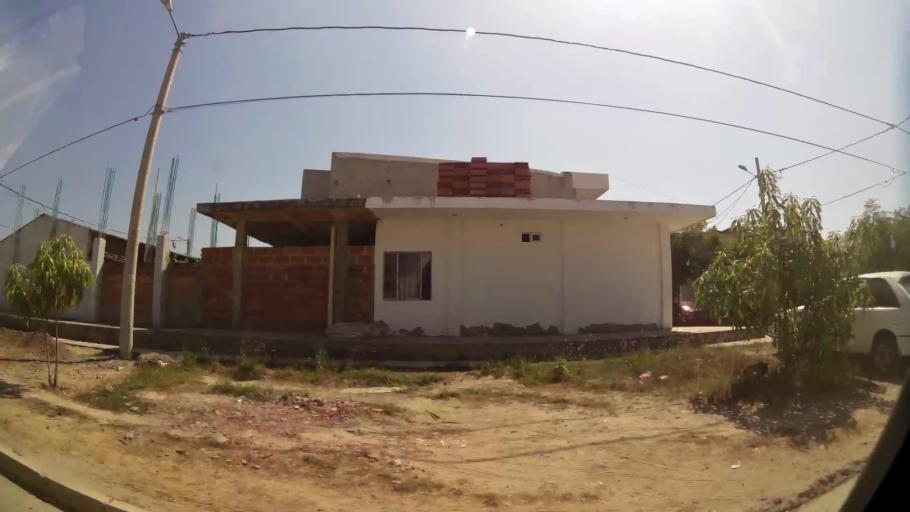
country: CO
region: Bolivar
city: Cartagena
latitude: 10.3932
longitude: -75.4493
